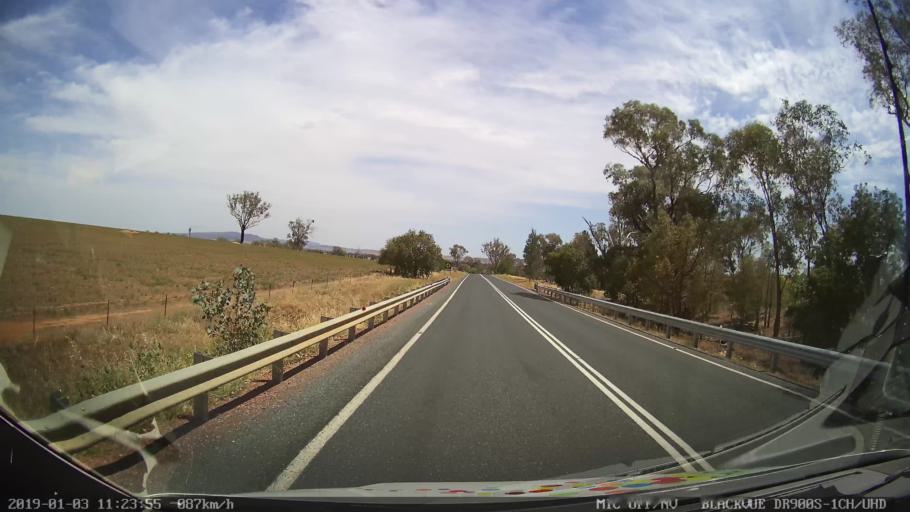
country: AU
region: New South Wales
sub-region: Weddin
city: Grenfell
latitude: -34.0577
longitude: 148.2389
